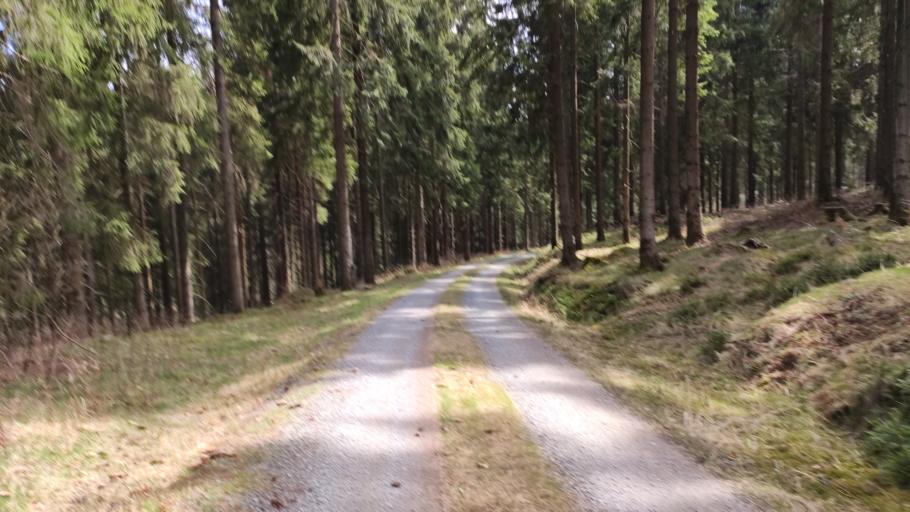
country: DE
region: Bavaria
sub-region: Upper Franconia
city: Reichenbach
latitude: 50.4446
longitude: 11.4356
